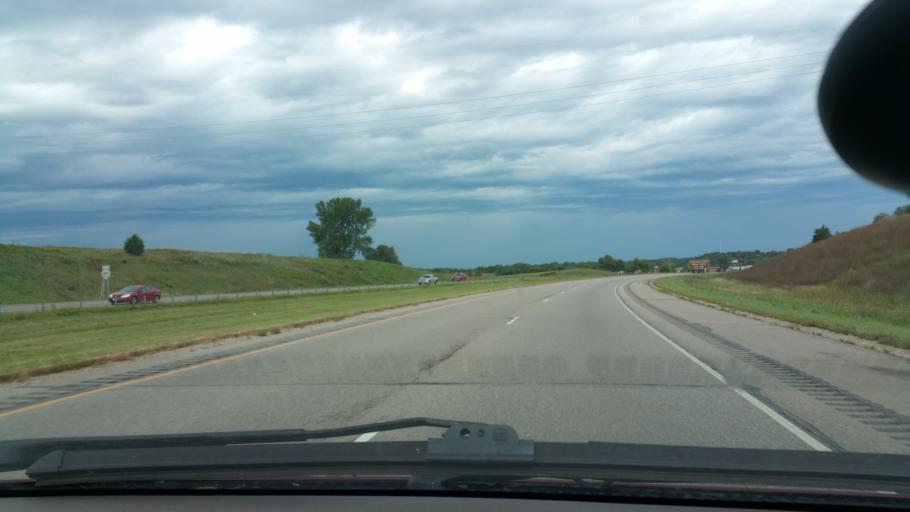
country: US
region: Minnesota
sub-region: Rice County
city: Faribault
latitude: 44.2829
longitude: -93.3075
